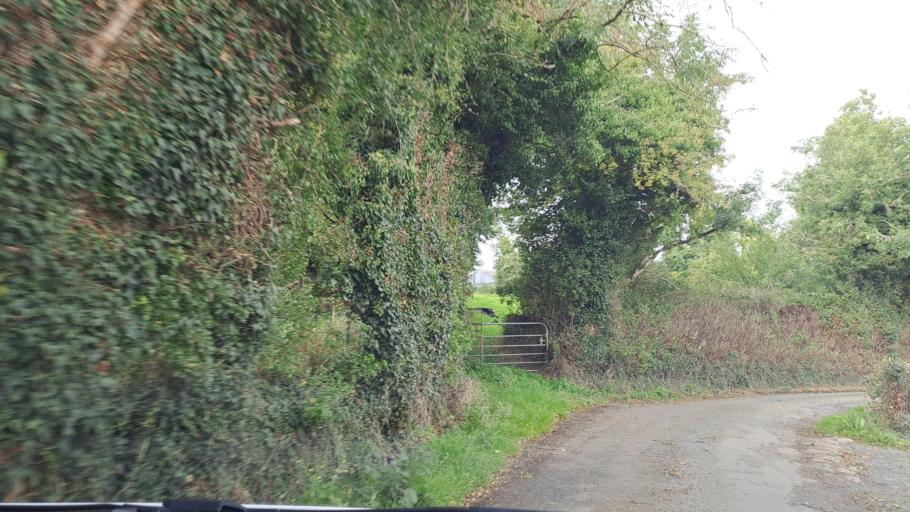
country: IE
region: Ulster
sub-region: An Cabhan
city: Bailieborough
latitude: 53.9956
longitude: -6.9390
